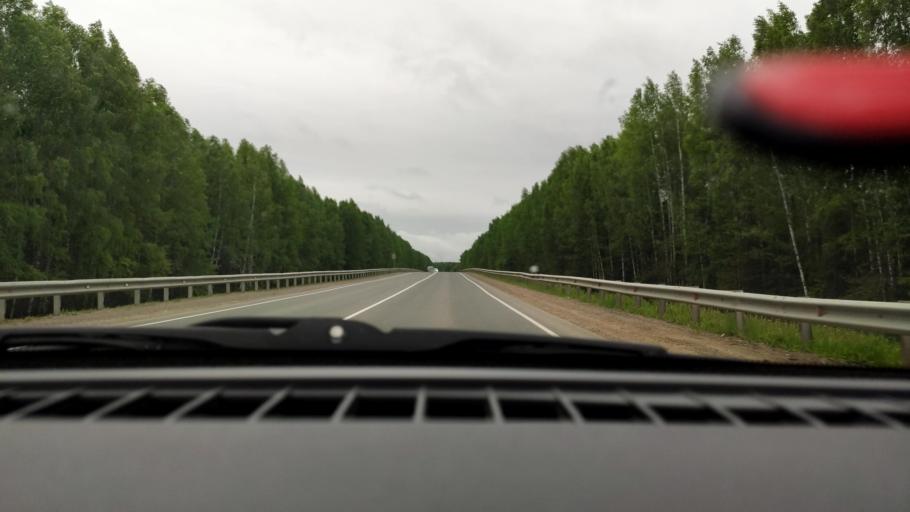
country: RU
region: Perm
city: Mendeleyevo
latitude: 58.2139
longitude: 54.9671
